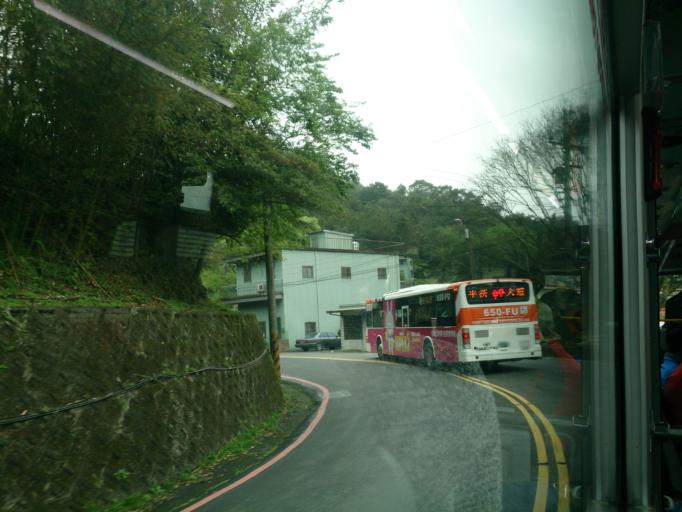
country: TW
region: Taiwan
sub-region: Keelung
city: Keelung
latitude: 25.0229
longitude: 121.7205
